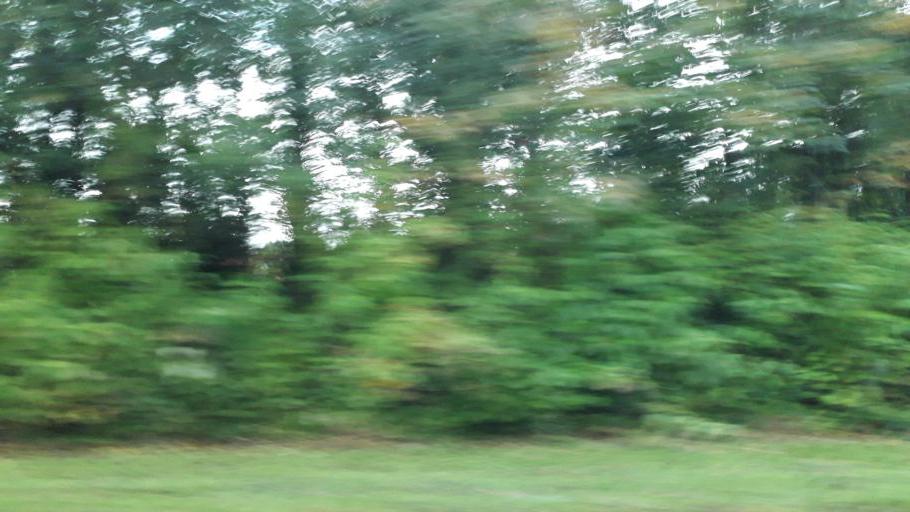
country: IE
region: Leinster
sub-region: An Longfort
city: Longford
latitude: 53.7240
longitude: -7.7655
